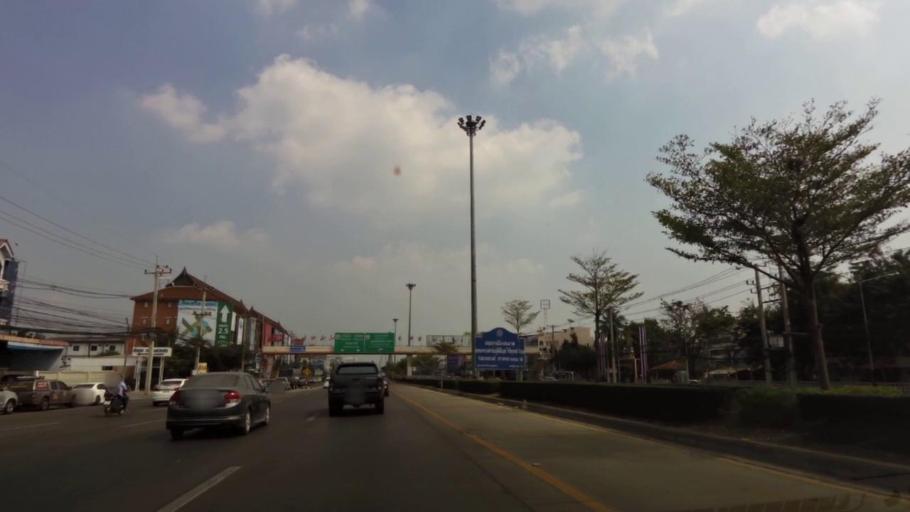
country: TH
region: Phra Nakhon Si Ayutthaya
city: Phra Nakhon Si Ayutthaya
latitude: 14.3532
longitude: 100.5877
